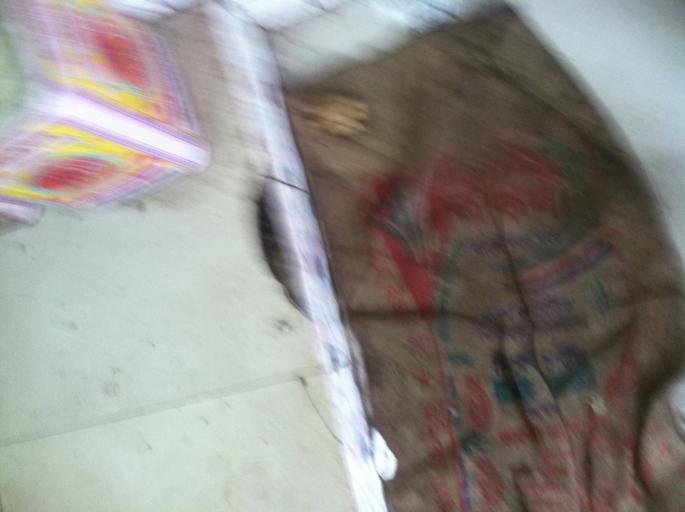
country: BD
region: Dhaka
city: Azimpur
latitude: 23.7169
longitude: 90.3861
